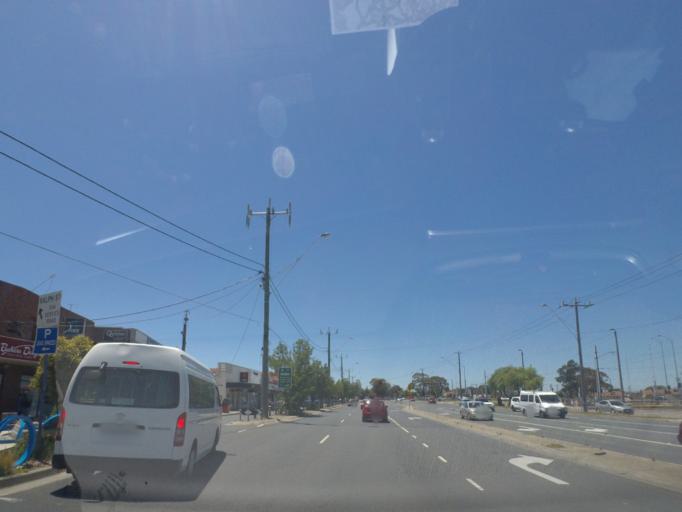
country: AU
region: Victoria
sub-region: Darebin
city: Reservoir
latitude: -37.7163
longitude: 145.0068
